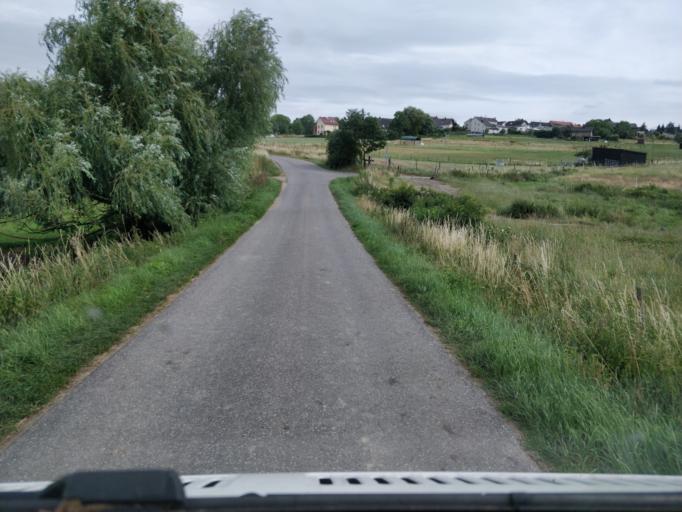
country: DE
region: North Rhine-Westphalia
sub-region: Regierungsbezirk Koln
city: Rheinbach
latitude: 50.5961
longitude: 6.9272
